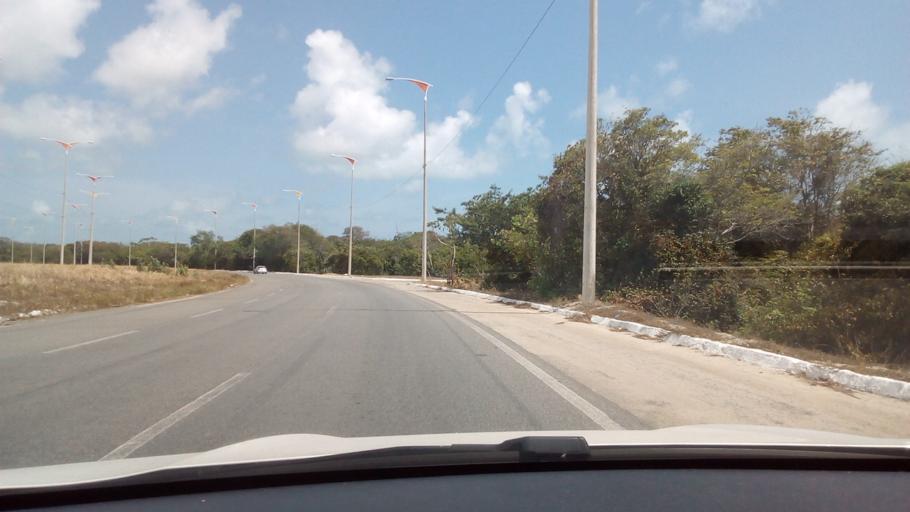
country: BR
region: Paraiba
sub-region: Joao Pessoa
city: Joao Pessoa
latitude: -7.1892
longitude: -34.8018
